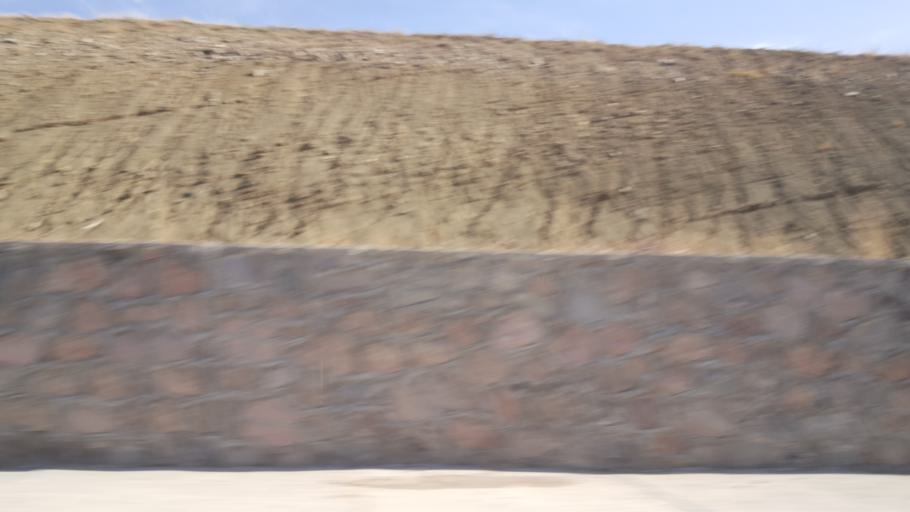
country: TR
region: Ankara
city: Yenice
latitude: 39.3684
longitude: 32.7160
